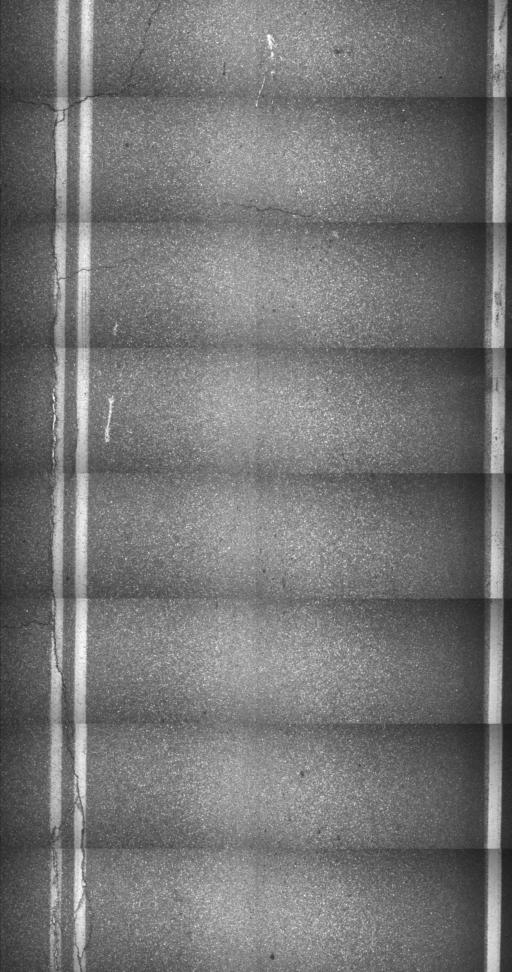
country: US
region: Vermont
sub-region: Orange County
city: Williamstown
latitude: 44.1133
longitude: -72.5763
